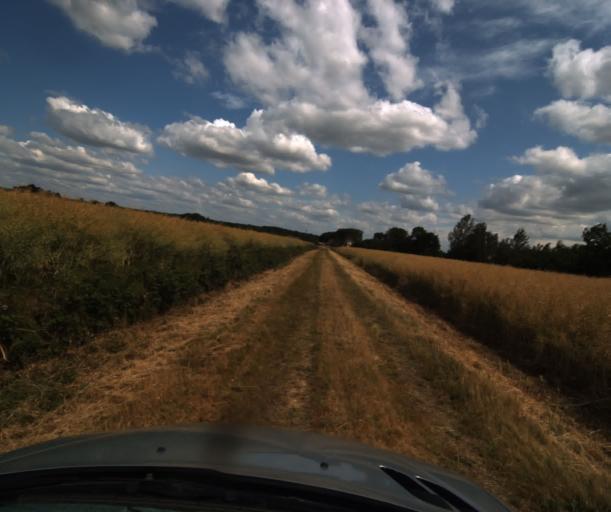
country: FR
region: Midi-Pyrenees
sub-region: Departement du Tarn-et-Garonne
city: Campsas
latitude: 43.9181
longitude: 1.2913
